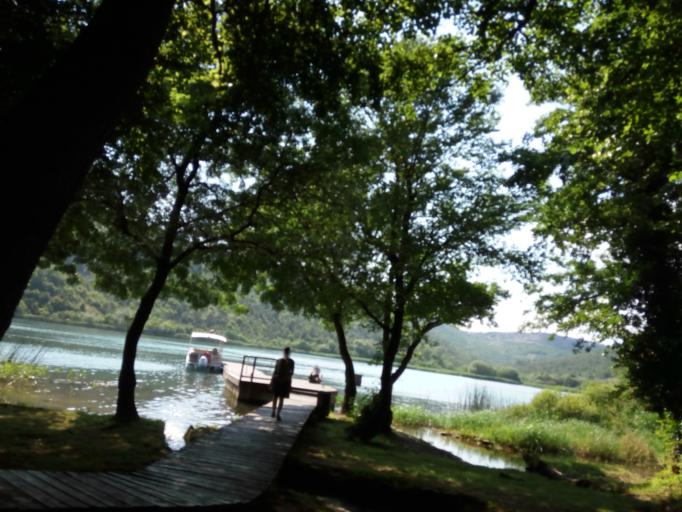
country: HR
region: Sibensko-Kniniska
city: Kistanje
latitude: 43.9023
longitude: 15.9761
